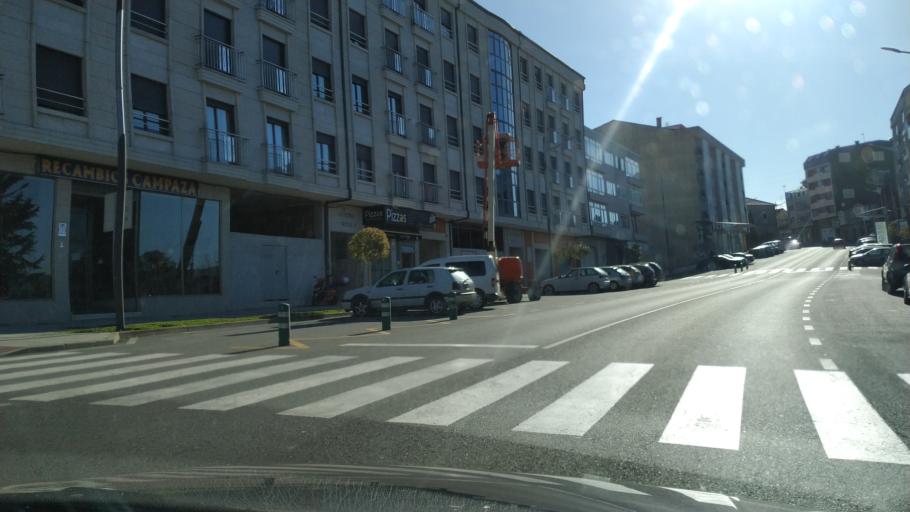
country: ES
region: Galicia
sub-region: Provincia de Pontevedra
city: Silleda
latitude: 42.6989
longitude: -8.2494
